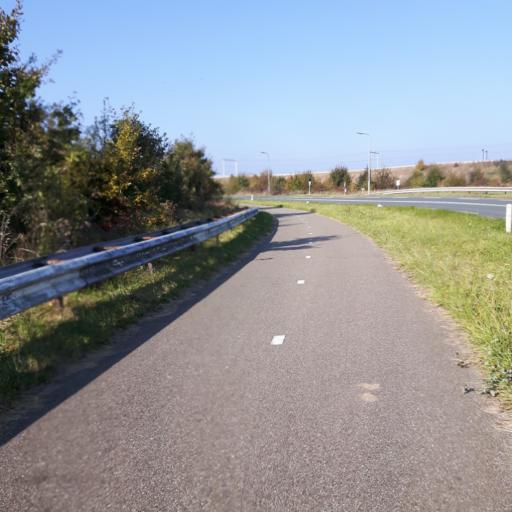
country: NL
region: Zeeland
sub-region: Gemeente Reimerswaal
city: Yerseke
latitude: 51.4677
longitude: 4.0040
